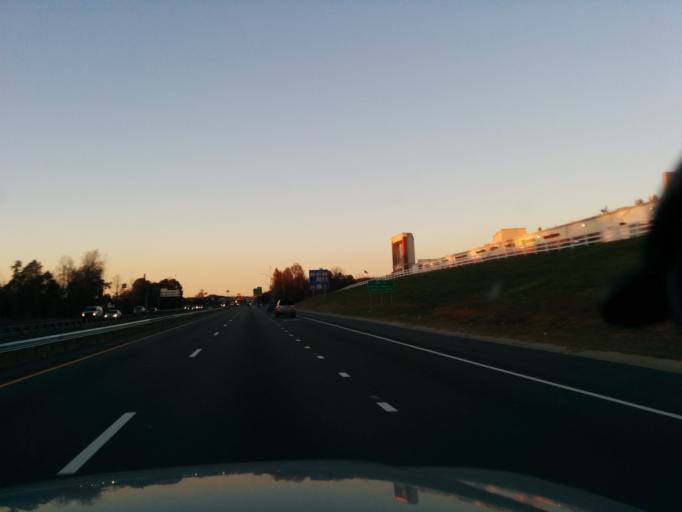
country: US
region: North Carolina
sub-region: Iredell County
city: Mooresville
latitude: 35.5882
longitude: -80.8584
